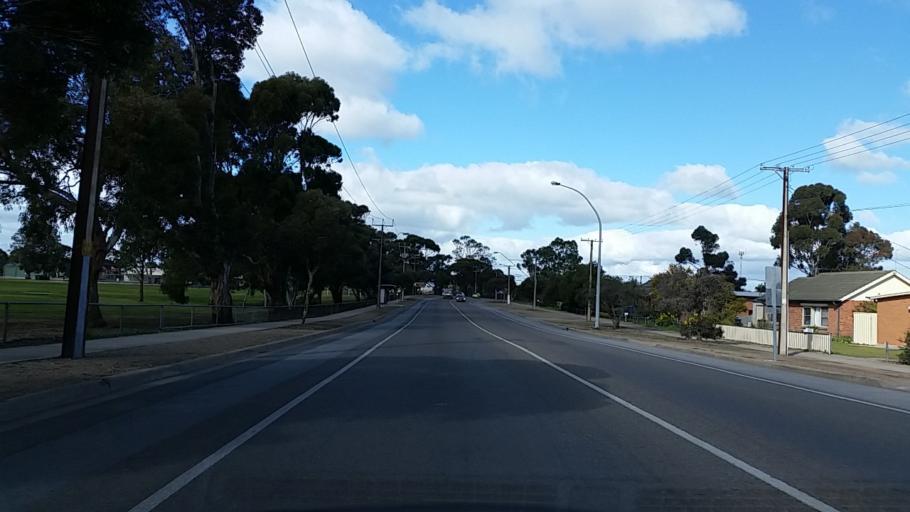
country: AU
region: South Australia
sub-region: Murray Bridge
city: Murray Bridge
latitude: -35.1351
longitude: 139.2830
